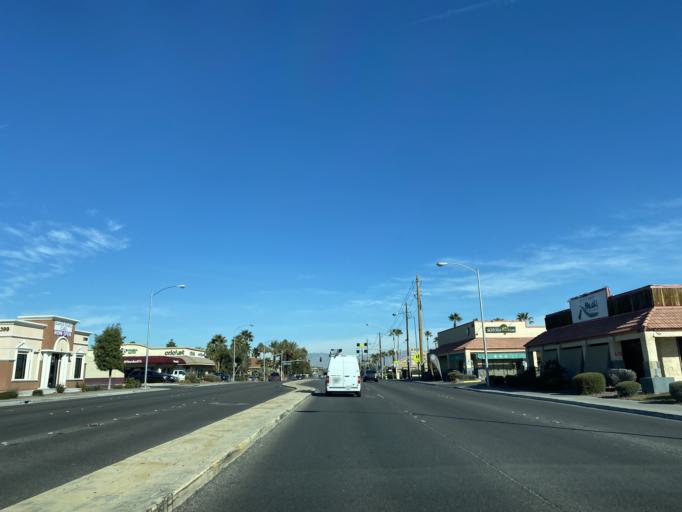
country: US
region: Nevada
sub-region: Clark County
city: Spring Valley
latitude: 36.1275
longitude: -115.2249
